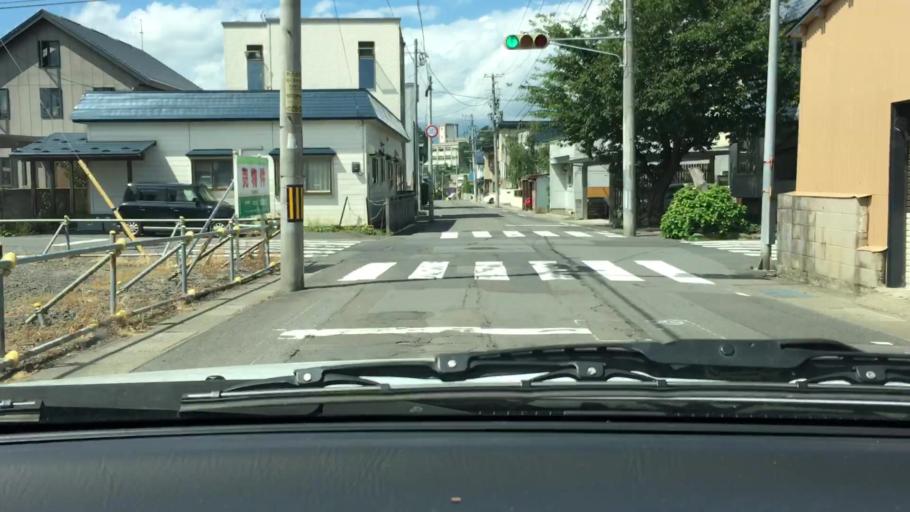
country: JP
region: Aomori
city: Hirosaki
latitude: 40.5936
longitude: 140.4723
